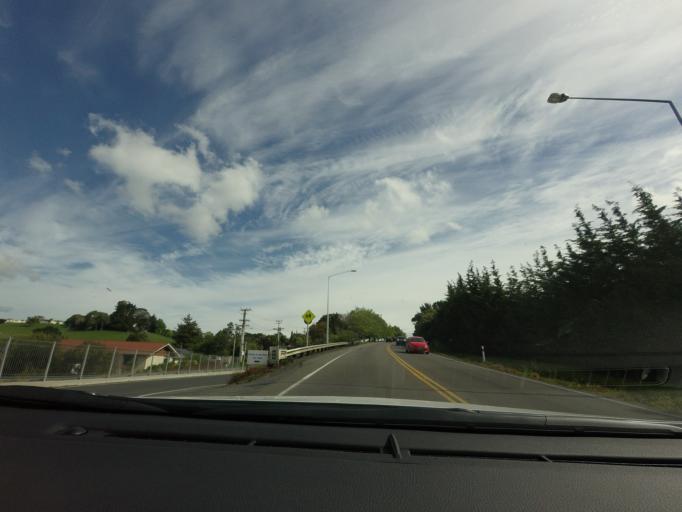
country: NZ
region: Auckland
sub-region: Auckland
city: Warkworth
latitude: -36.4103
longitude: 174.6589
